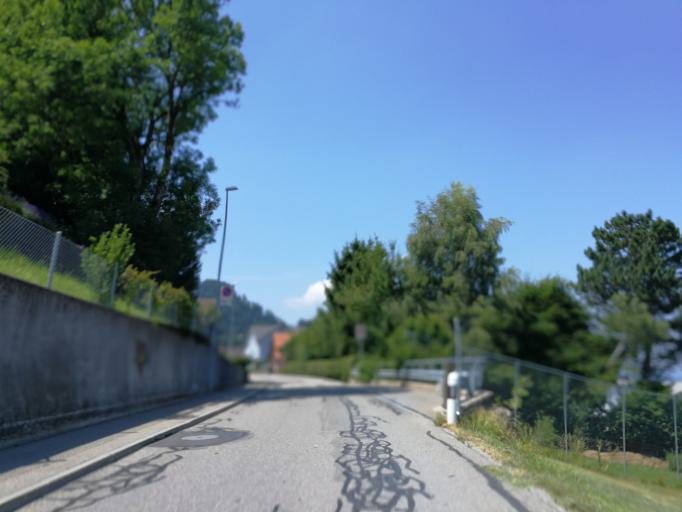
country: CH
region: Schwyz
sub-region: Bezirk Hoefe
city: Schindellegi
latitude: 47.1751
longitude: 8.7168
